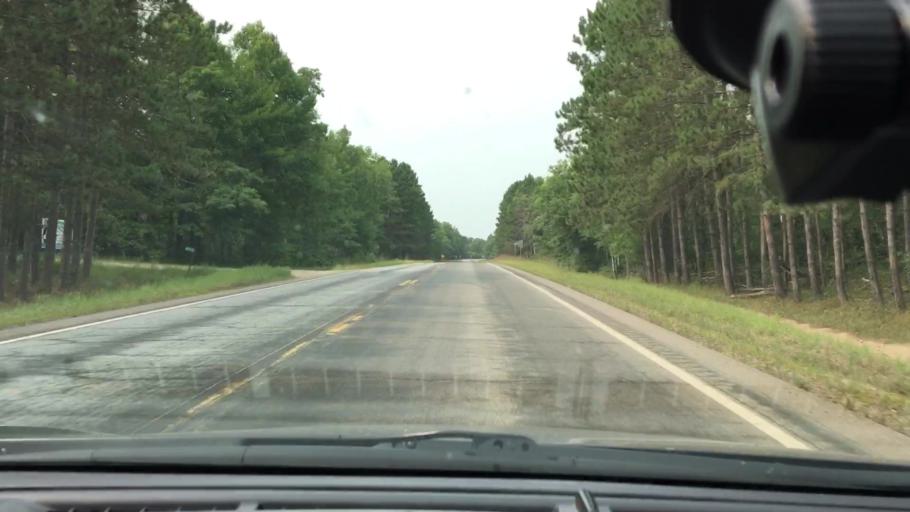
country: US
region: Minnesota
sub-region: Crow Wing County
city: Cross Lake
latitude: 46.7380
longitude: -93.9625
